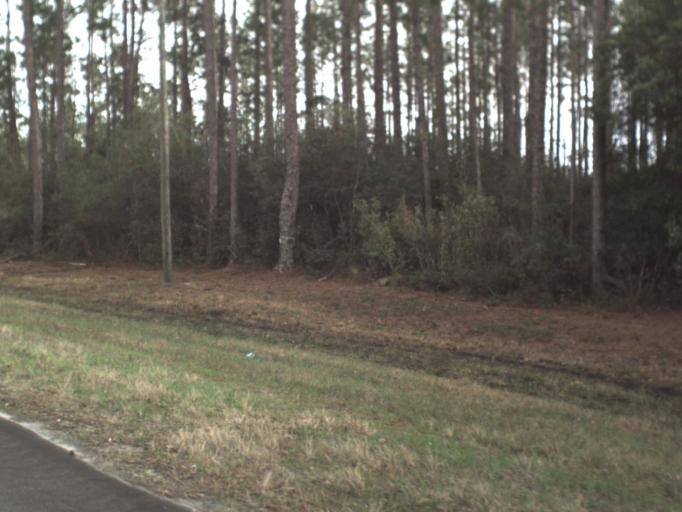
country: US
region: Florida
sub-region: Gulf County
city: Wewahitchka
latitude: 30.1366
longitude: -85.3763
